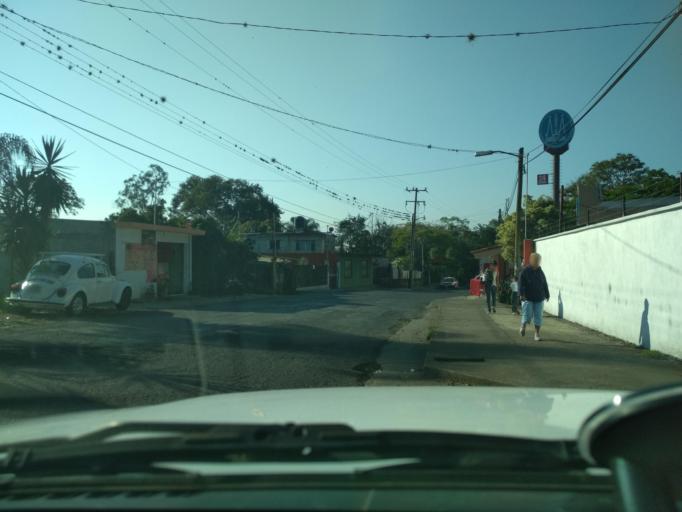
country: MX
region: Veracruz
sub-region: Fortin
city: Fraccionamiento Villas de la Llave
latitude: 18.9186
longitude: -96.9901
